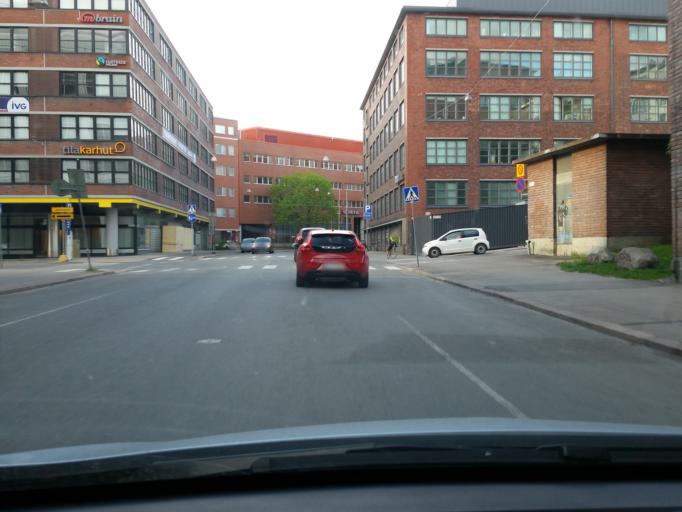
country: FI
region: Uusimaa
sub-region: Helsinki
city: Helsinki
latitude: 60.1959
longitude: 24.9478
